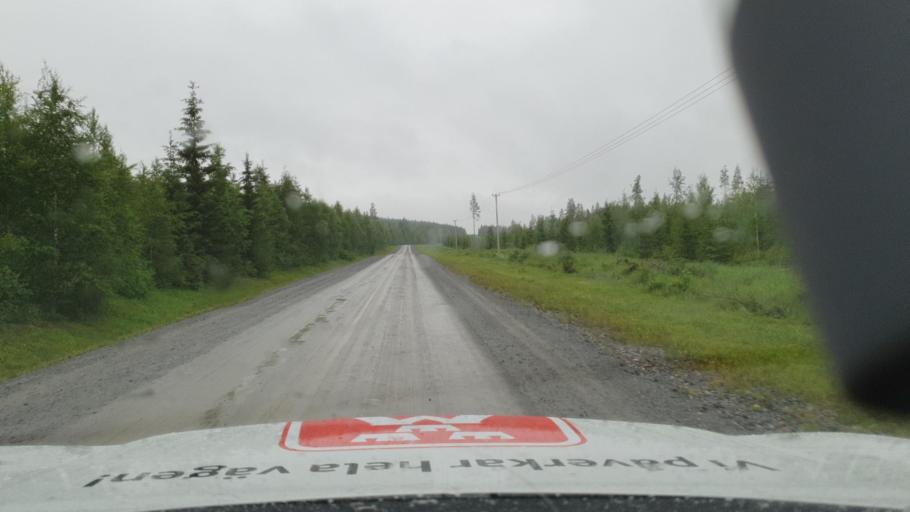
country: SE
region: Vaesterbotten
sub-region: Bjurholms Kommun
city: Bjurholm
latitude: 63.8875
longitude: 19.4258
